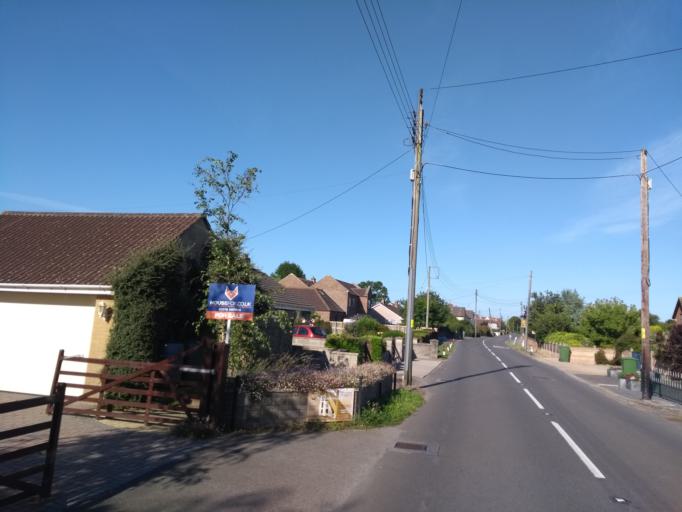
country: GB
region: England
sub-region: Somerset
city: Woolavington
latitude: 51.2234
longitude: -2.9198
